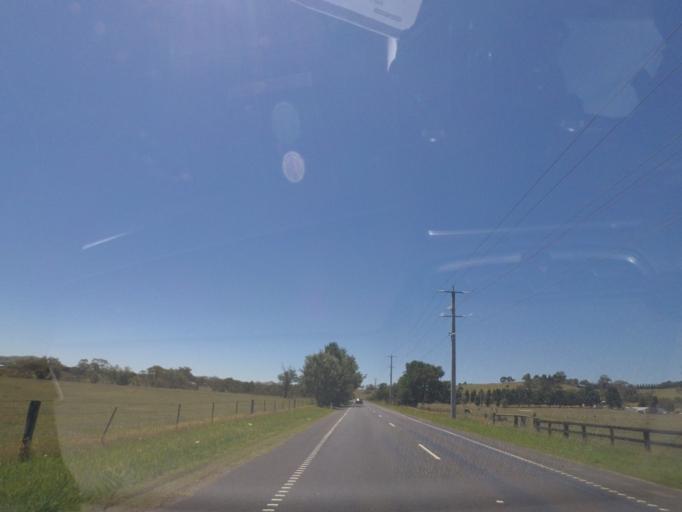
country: AU
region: Victoria
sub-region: Whittlesea
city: Whittlesea
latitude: -37.4962
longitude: 145.0259
